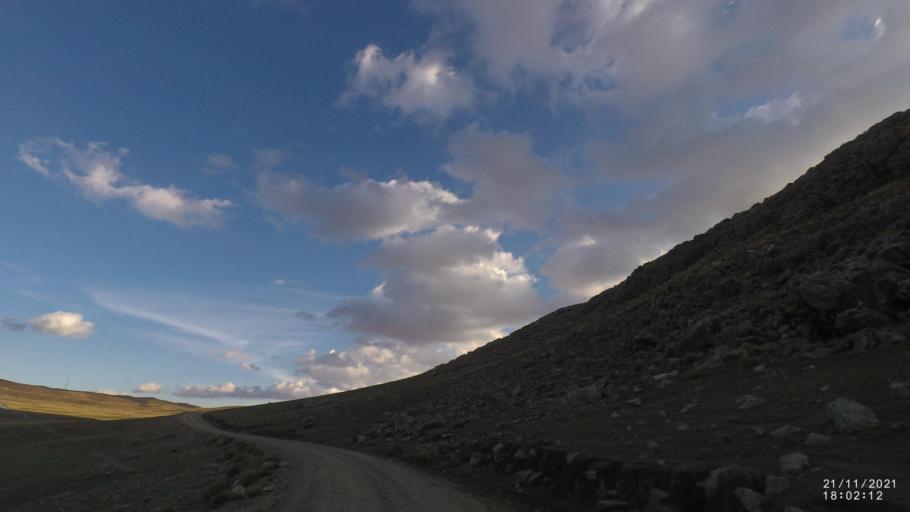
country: BO
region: Cochabamba
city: Cochabamba
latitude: -17.2529
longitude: -66.2283
